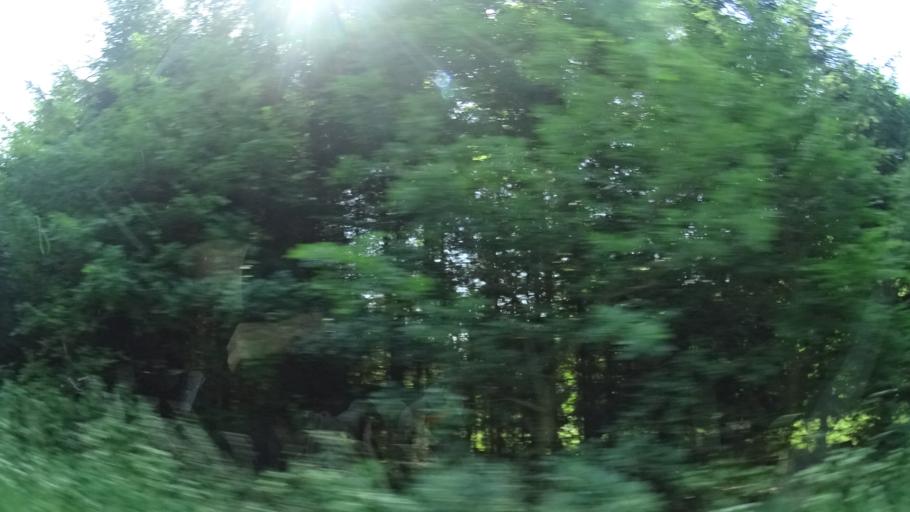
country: DE
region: Hesse
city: Rosenthal
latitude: 50.9360
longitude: 8.8429
